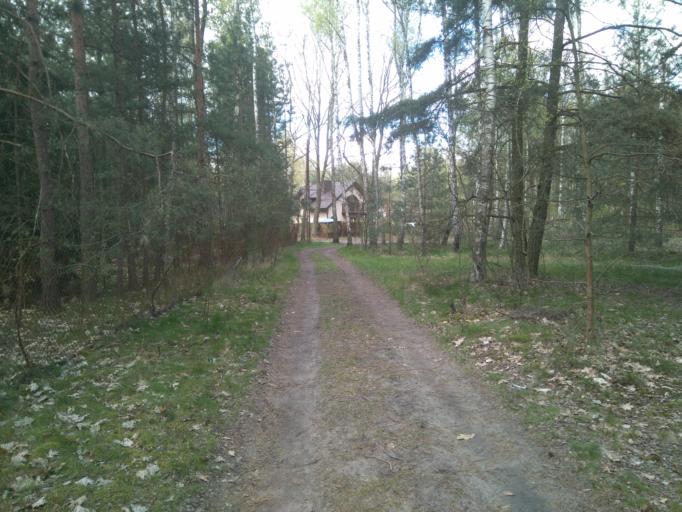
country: PL
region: Masovian Voivodeship
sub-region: Powiat zyrardowski
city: Radziejowice
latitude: 52.0682
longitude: 20.5694
